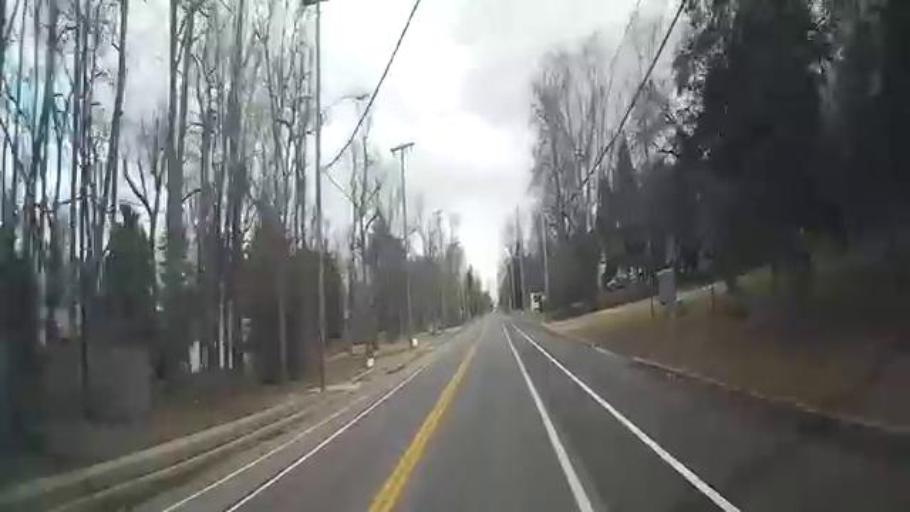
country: US
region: New Jersey
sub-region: Camden County
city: Clementon
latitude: 39.7998
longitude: -74.9621
